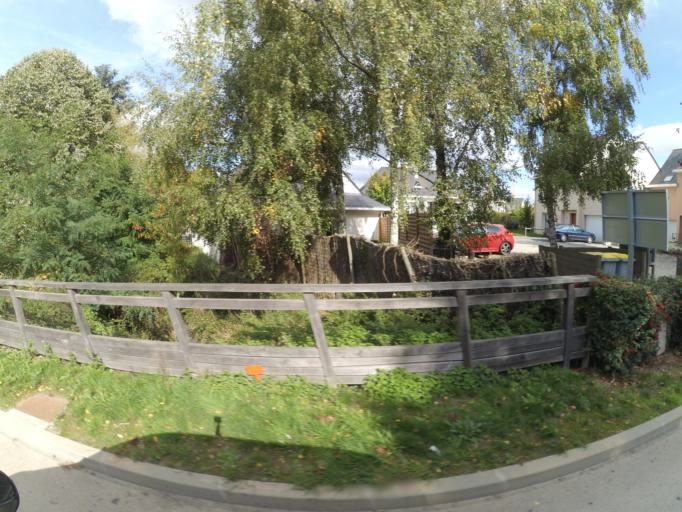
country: FR
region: Pays de la Loire
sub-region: Departement de la Loire-Atlantique
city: Thouare-sur-Loire
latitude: 47.2749
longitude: -1.4464
